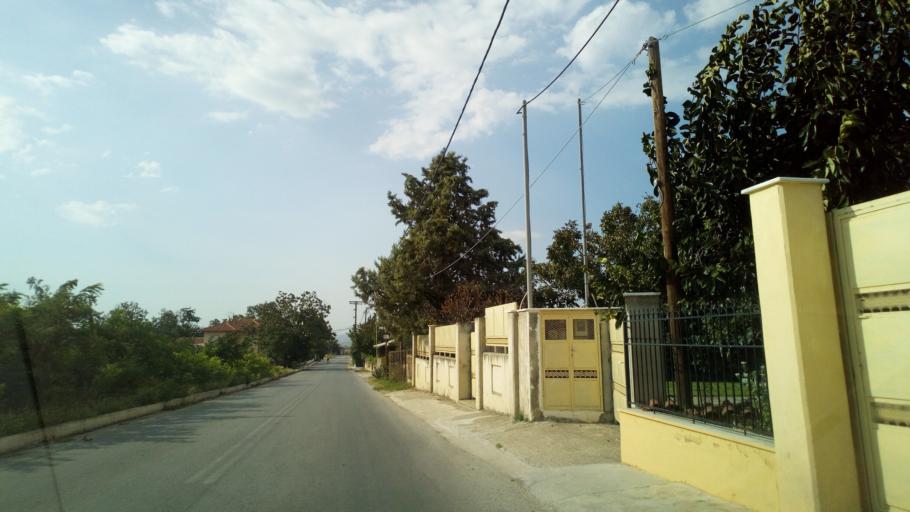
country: GR
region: Central Macedonia
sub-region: Nomos Thessalonikis
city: Gerakarou
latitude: 40.6288
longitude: 23.2186
